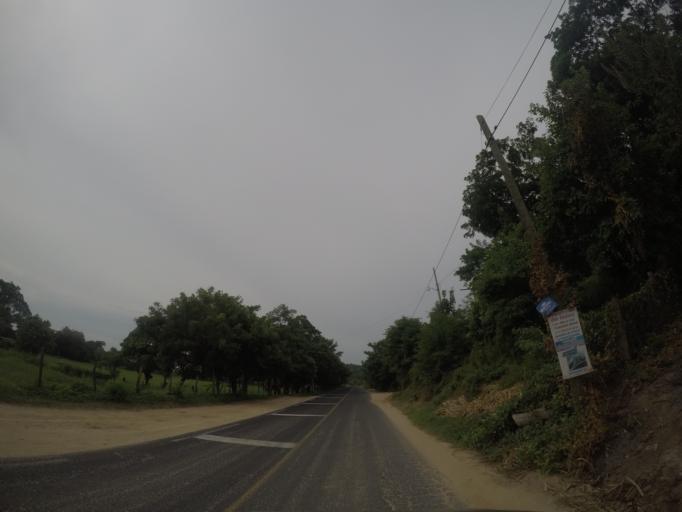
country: MX
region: Oaxaca
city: San Pedro Mixtepec
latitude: 15.9551
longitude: -97.2525
